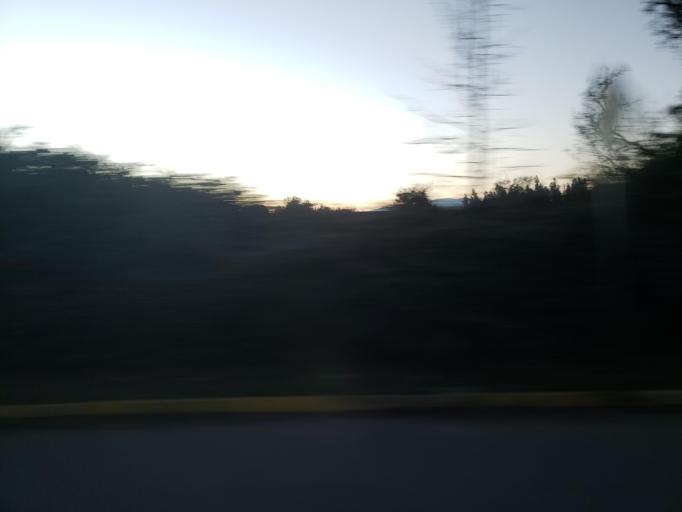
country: CL
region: Santiago Metropolitan
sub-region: Provincia de Talagante
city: El Monte
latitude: -33.6868
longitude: -70.9701
